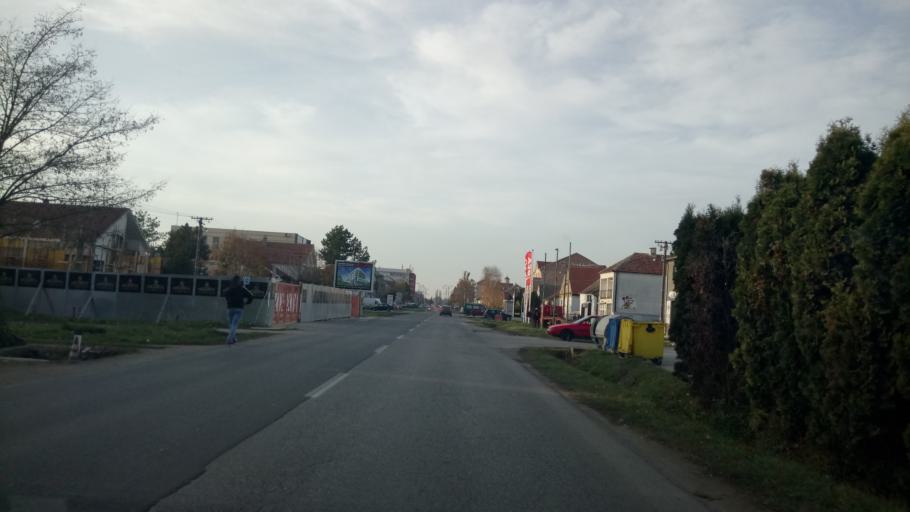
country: RS
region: Autonomna Pokrajina Vojvodina
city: Nova Pazova
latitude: 44.9420
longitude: 20.2227
